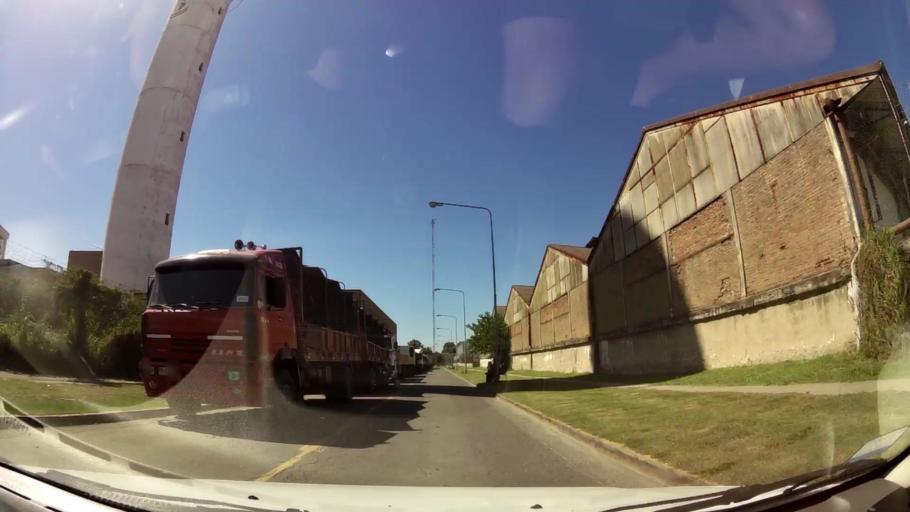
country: AR
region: Buenos Aires F.D.
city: Buenos Aires
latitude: -34.6255
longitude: -58.3528
